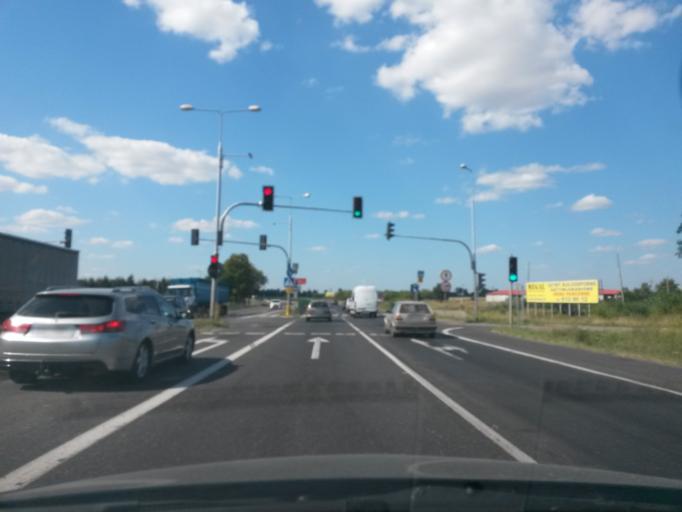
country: PL
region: Masovian Voivodeship
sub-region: Powiat plonski
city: Zaluski
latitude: 52.4762
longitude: 20.5645
